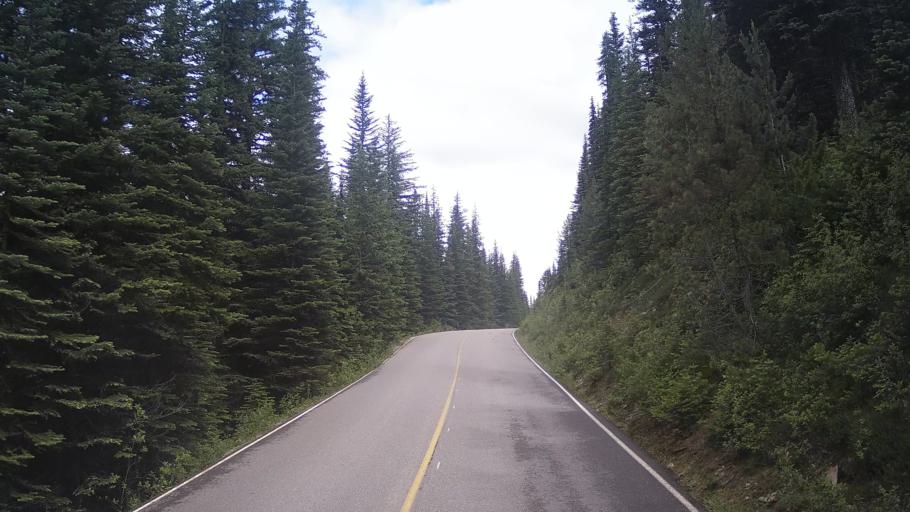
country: CA
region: Alberta
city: Jasper Park Lodge
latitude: 52.6917
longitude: -118.0575
